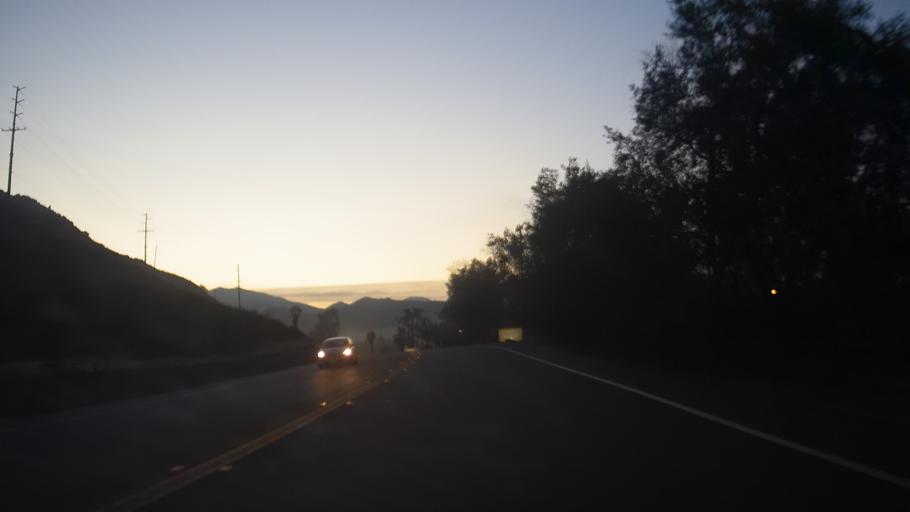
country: US
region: California
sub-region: San Diego County
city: Granite Hills
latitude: 32.7877
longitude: -116.8863
